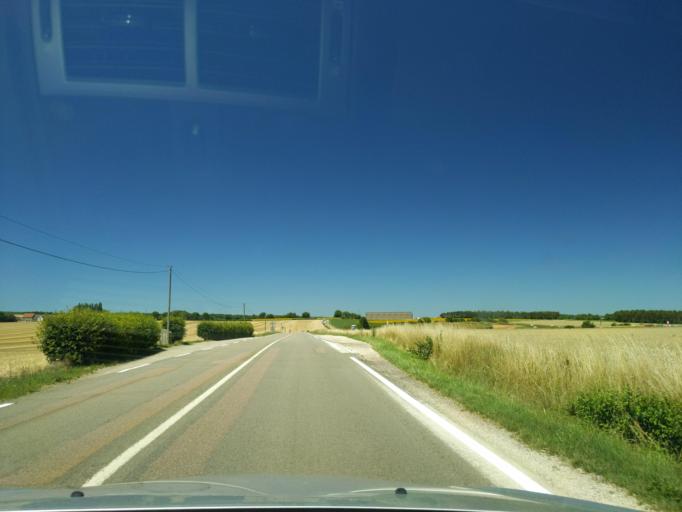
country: FR
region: Bourgogne
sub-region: Departement de la Cote-d'Or
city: Is-sur-Tille
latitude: 47.4964
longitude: 5.0913
